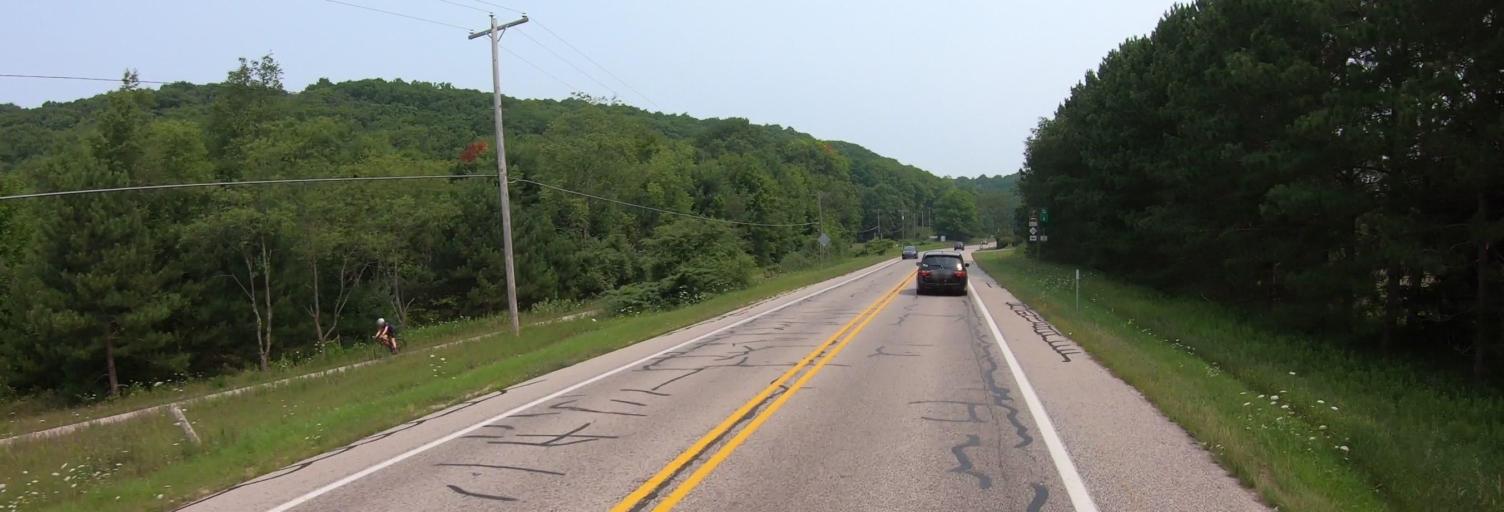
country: US
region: Michigan
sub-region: Benzie County
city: Beulah
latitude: 44.8316
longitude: -86.0371
